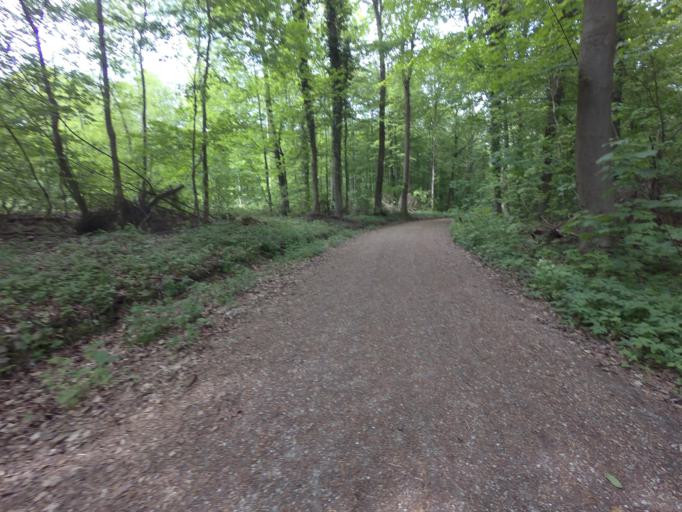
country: DE
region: Lower Saxony
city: Diekholzen
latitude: 52.1251
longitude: 9.9027
